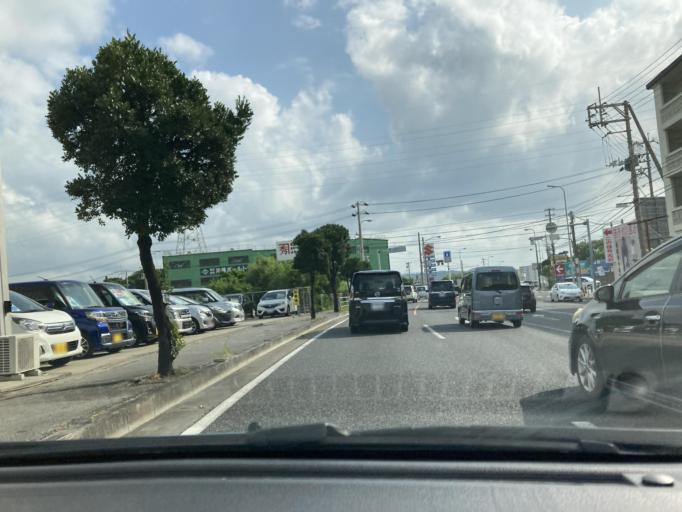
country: JP
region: Okinawa
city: Ginowan
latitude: 26.2334
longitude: 127.7698
